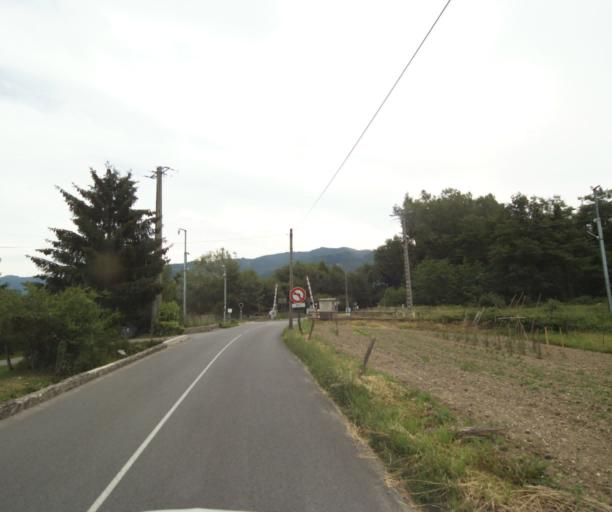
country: FR
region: Rhone-Alpes
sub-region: Departement de la Haute-Savoie
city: Perrignier
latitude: 46.2999
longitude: 6.4196
